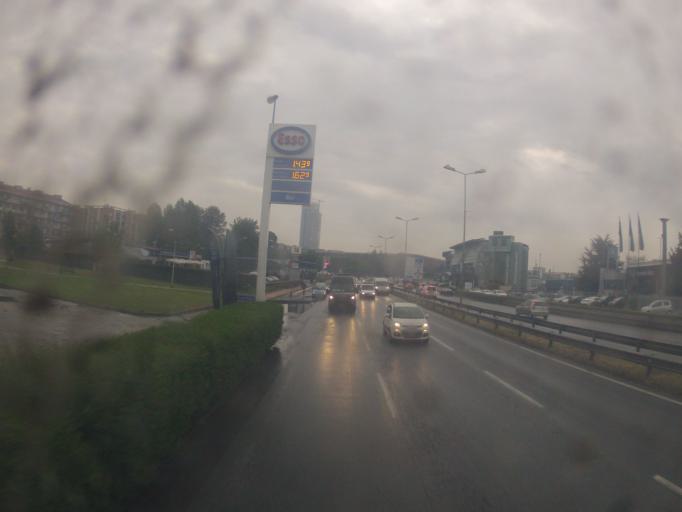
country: IT
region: Piedmont
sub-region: Provincia di Torino
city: Moncalieri
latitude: 45.0143
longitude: 7.6690
